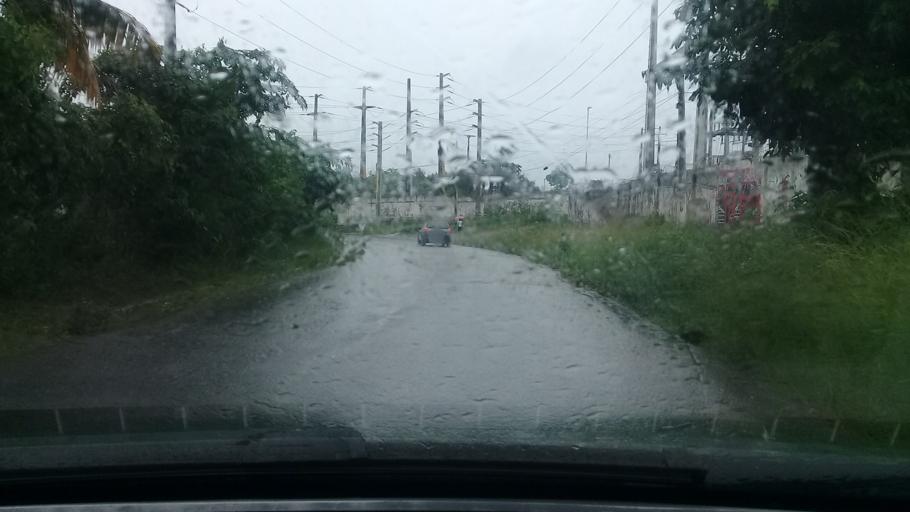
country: BR
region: Pernambuco
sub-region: Paulista
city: Paulista
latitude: -7.9561
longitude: -34.8911
